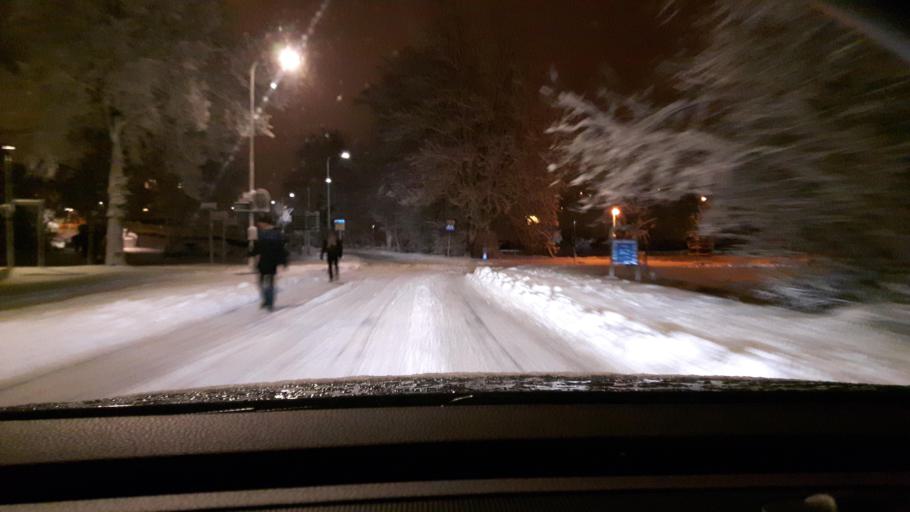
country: SE
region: Vaestra Goetaland
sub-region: Goteborg
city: Majorna
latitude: 57.6786
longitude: 11.8942
